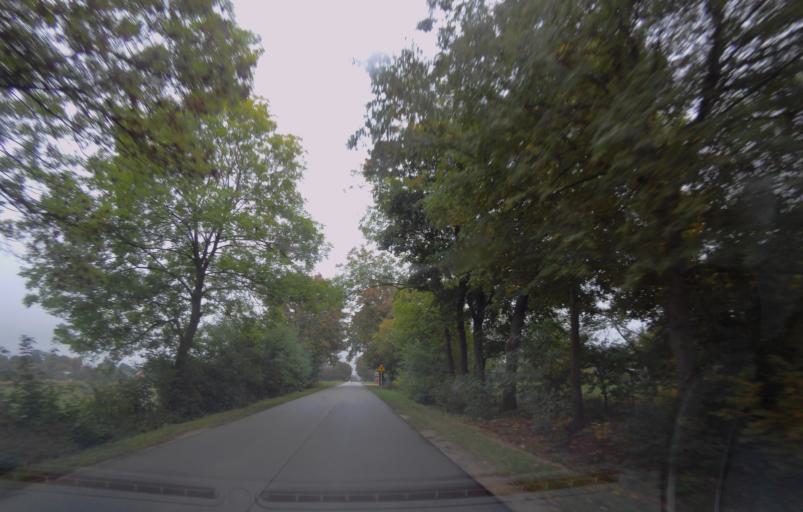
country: PL
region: Lublin Voivodeship
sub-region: Powiat chelmski
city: Sawin
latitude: 51.2140
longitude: 23.4488
